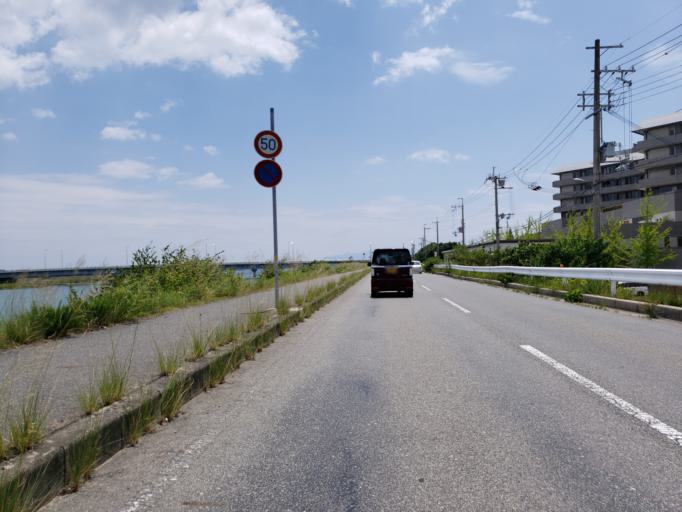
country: JP
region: Hyogo
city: Kariya
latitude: 34.7441
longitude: 134.3920
